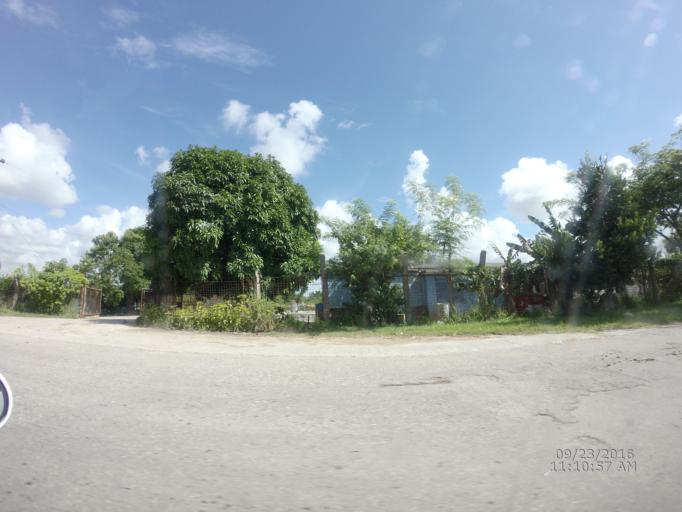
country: CU
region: La Habana
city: Arroyo Naranjo
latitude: 23.0234
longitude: -82.2627
